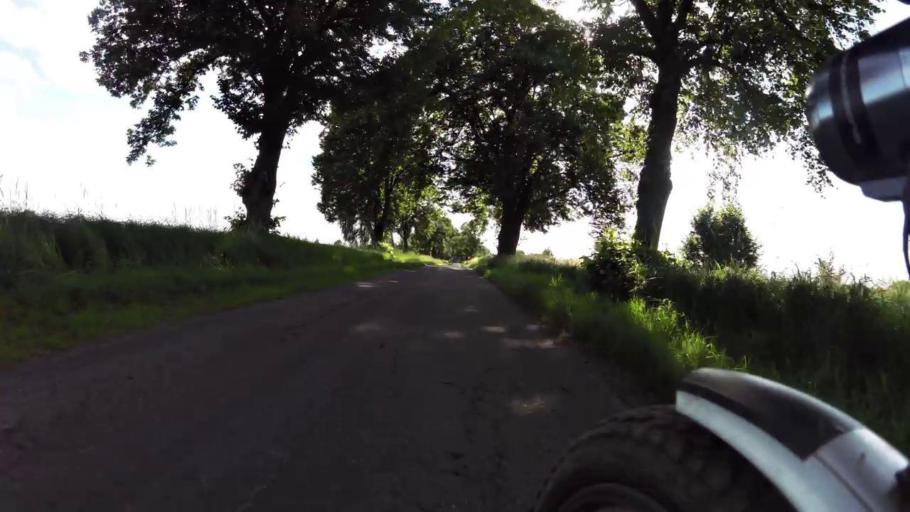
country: PL
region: West Pomeranian Voivodeship
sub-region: Powiat lobeski
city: Wegorzyno
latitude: 53.5386
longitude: 15.4403
